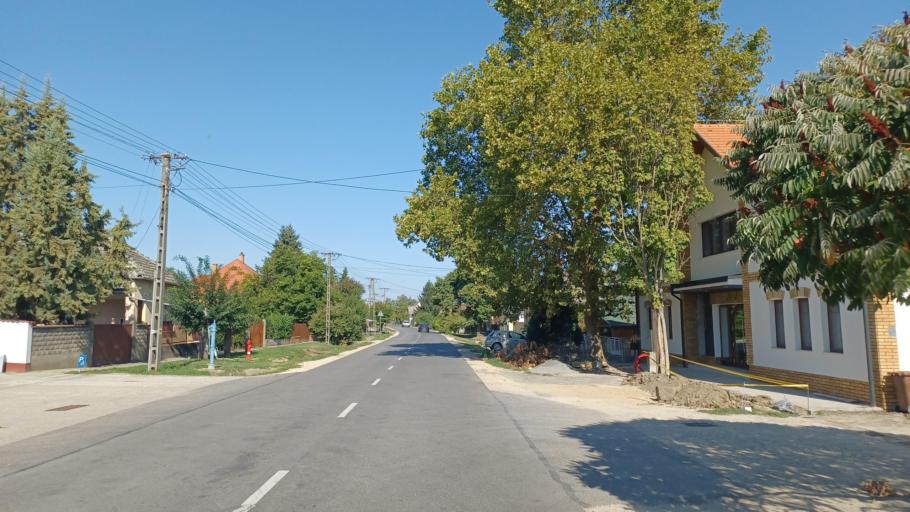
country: HU
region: Tolna
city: Nemetker
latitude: 46.7195
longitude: 18.7619
